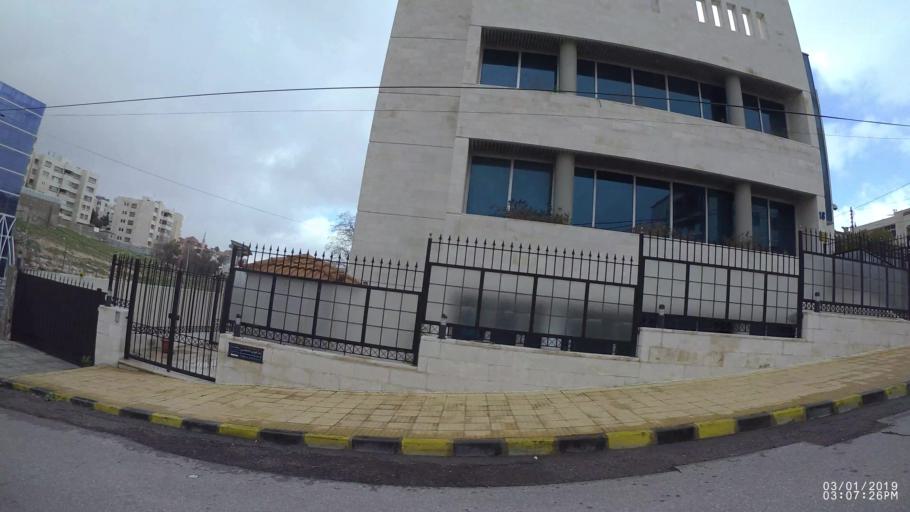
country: JO
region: Amman
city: Amman
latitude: 31.9547
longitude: 35.8844
